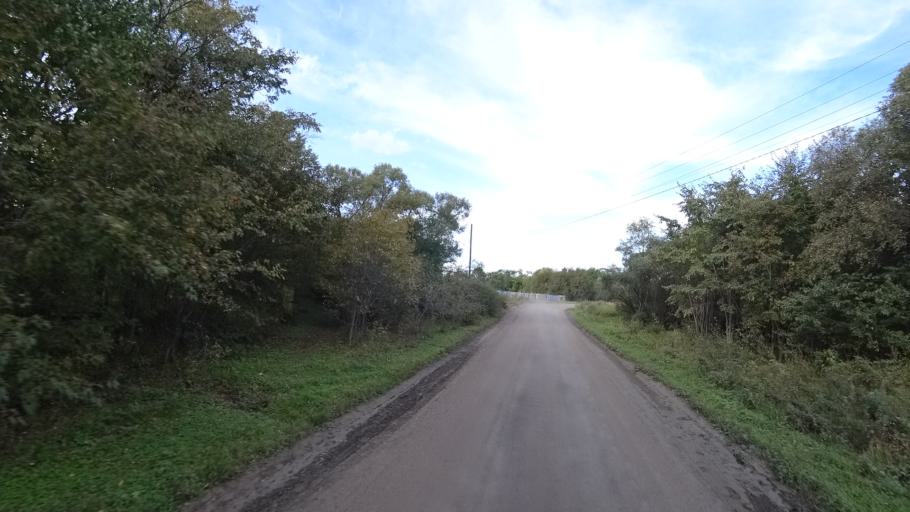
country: RU
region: Amur
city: Arkhara
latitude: 49.3550
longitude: 130.1102
